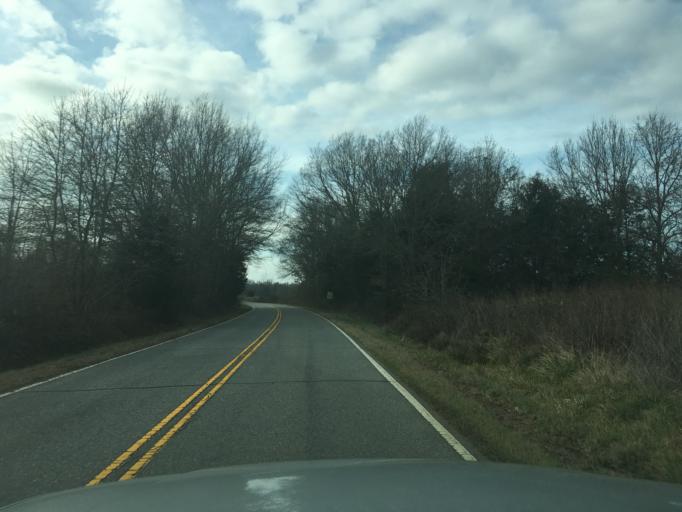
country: US
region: South Carolina
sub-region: Abbeville County
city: Lake Secession
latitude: 34.3576
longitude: -82.5088
